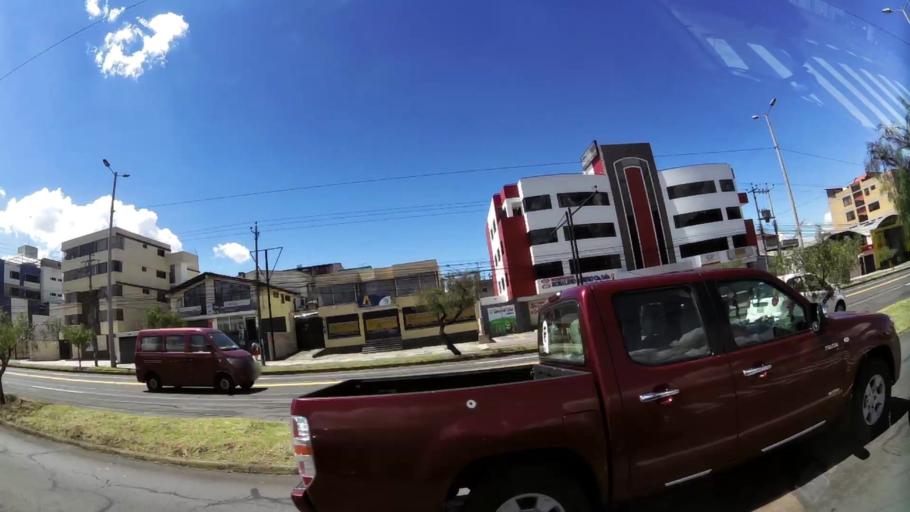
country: EC
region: Pichincha
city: Quito
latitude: -0.1368
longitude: -78.4824
